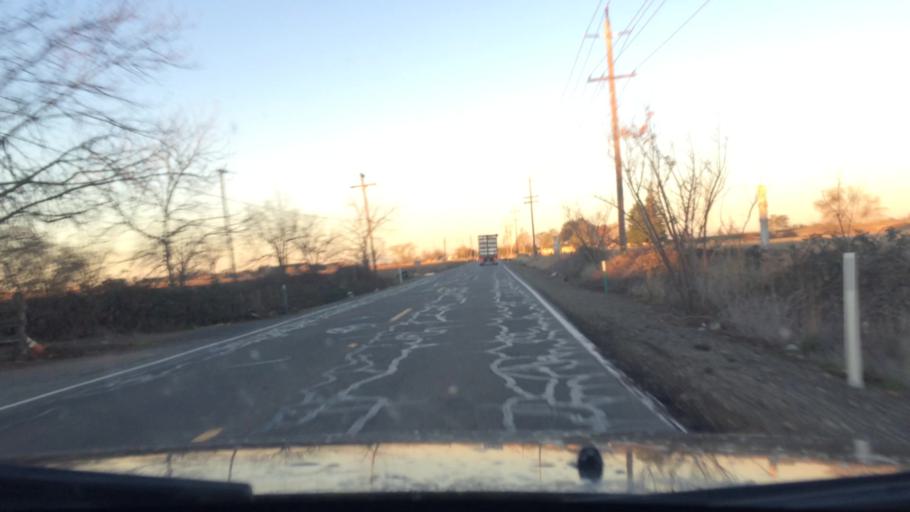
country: US
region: California
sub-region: Sacramento County
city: Vineyard
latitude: 38.5109
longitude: -121.3086
